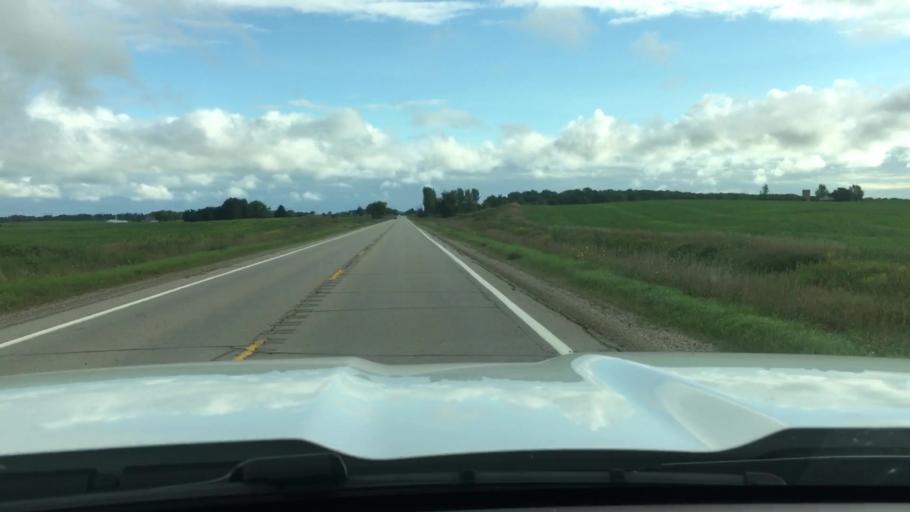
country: US
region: Michigan
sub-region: Tuscola County
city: Caro
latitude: 43.5711
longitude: -83.2998
